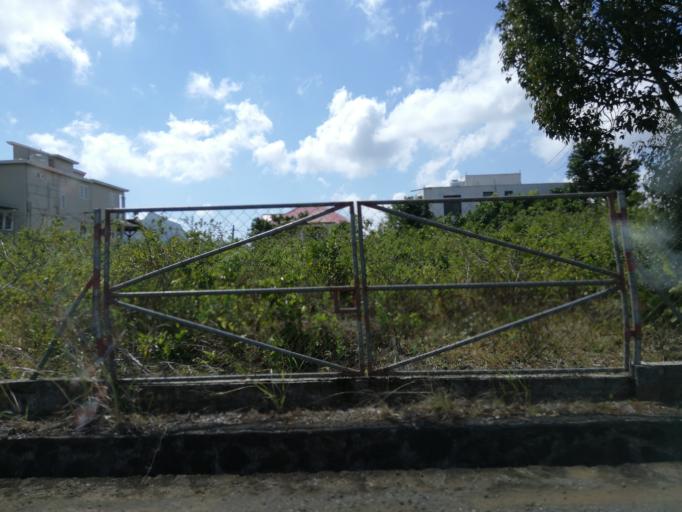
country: MU
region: Moka
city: Verdun
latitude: -20.2269
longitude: 57.5439
